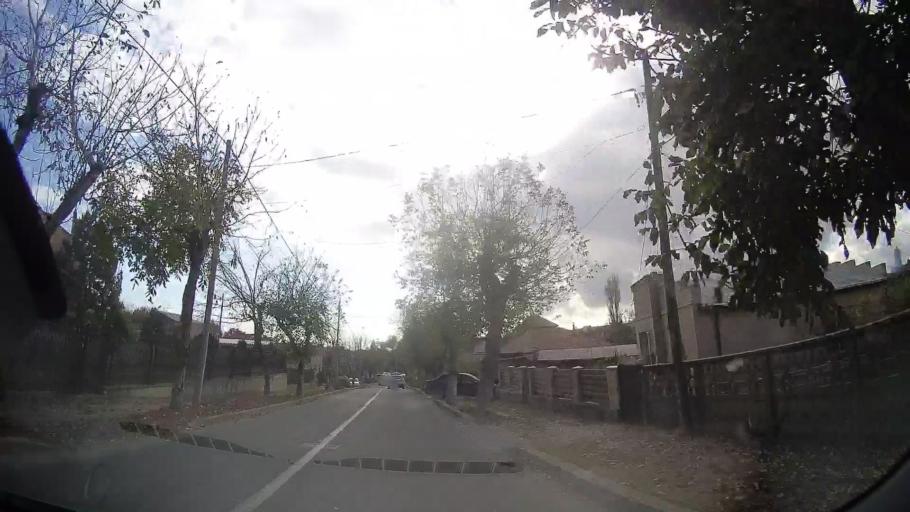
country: RO
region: Constanta
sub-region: Oras Techirghiol
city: Techirghiol
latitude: 44.0570
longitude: 28.6003
